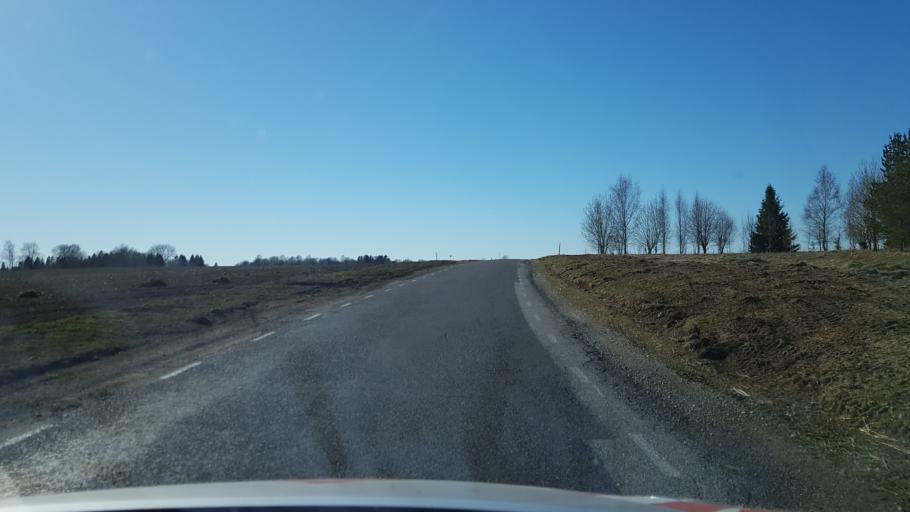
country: EE
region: Laeaene-Virumaa
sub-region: Haljala vald
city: Haljala
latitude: 59.4356
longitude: 26.1863
